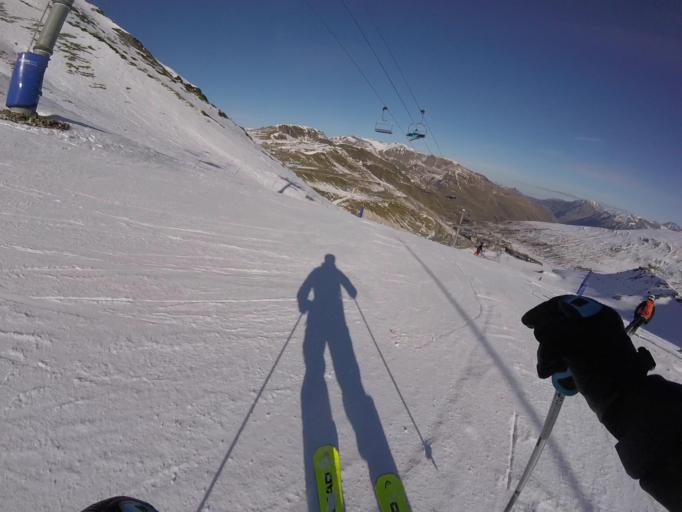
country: AD
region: Encamp
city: Pas de la Casa
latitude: 42.5301
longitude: 1.7228
